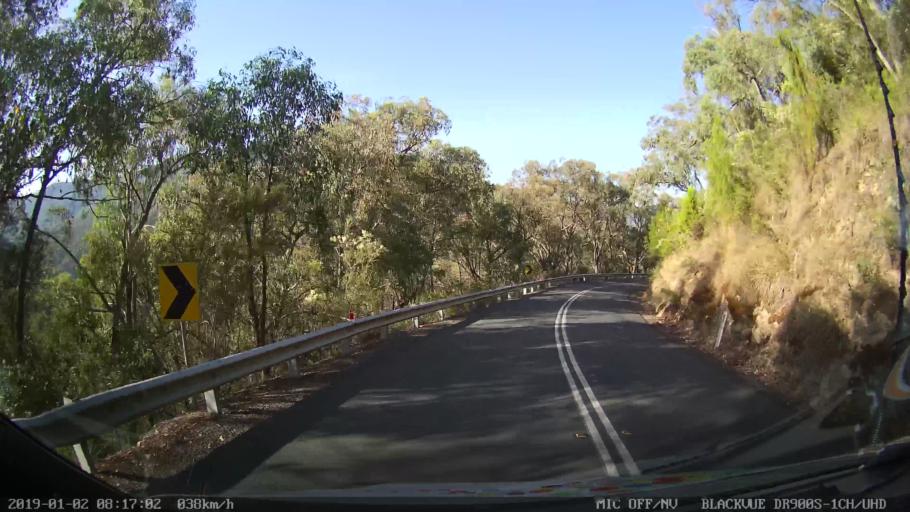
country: AU
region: New South Wales
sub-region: Tumut Shire
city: Tumut
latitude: -35.5809
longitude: 148.3268
